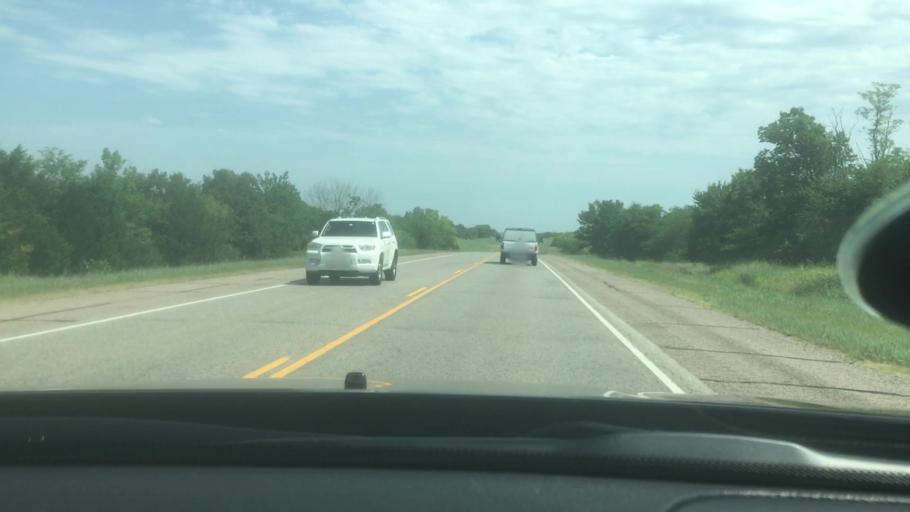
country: US
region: Oklahoma
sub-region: Seminole County
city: Maud
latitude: 35.0477
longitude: -96.9315
